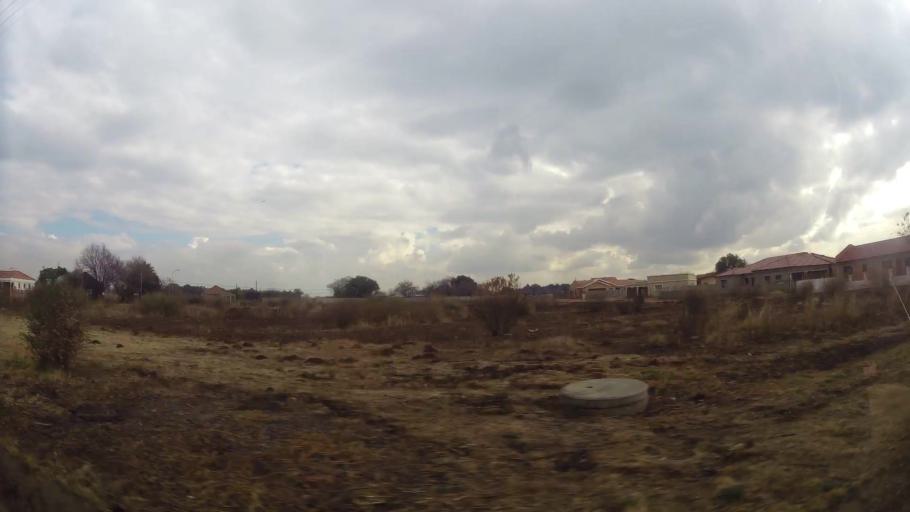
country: ZA
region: Gauteng
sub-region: Sedibeng District Municipality
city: Meyerton
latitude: -26.5892
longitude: 27.9960
